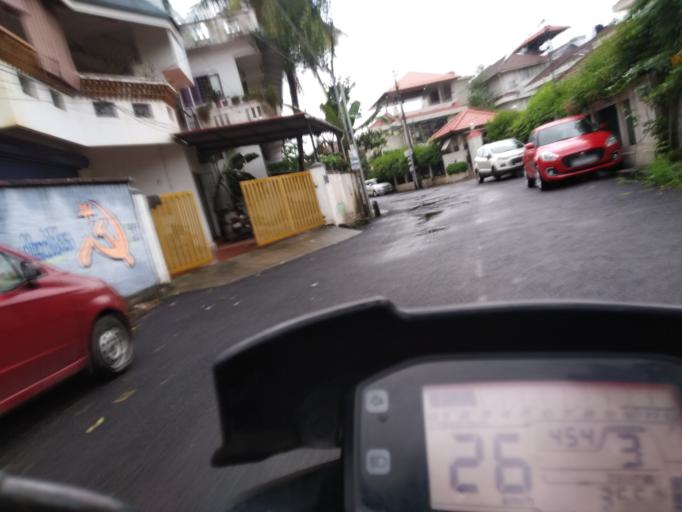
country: IN
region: Kerala
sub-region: Ernakulam
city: Cochin
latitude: 9.9740
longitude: 76.3088
